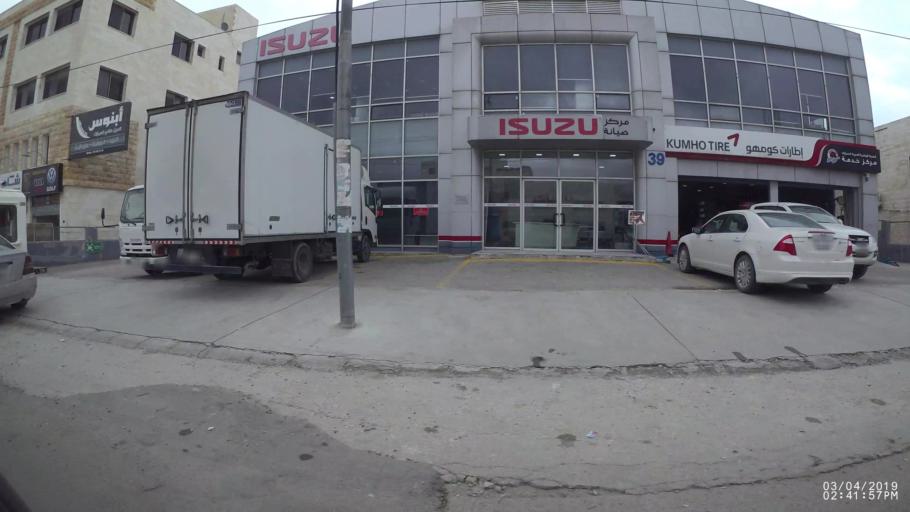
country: JO
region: Amman
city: Wadi as Sir
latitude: 31.9402
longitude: 35.8429
